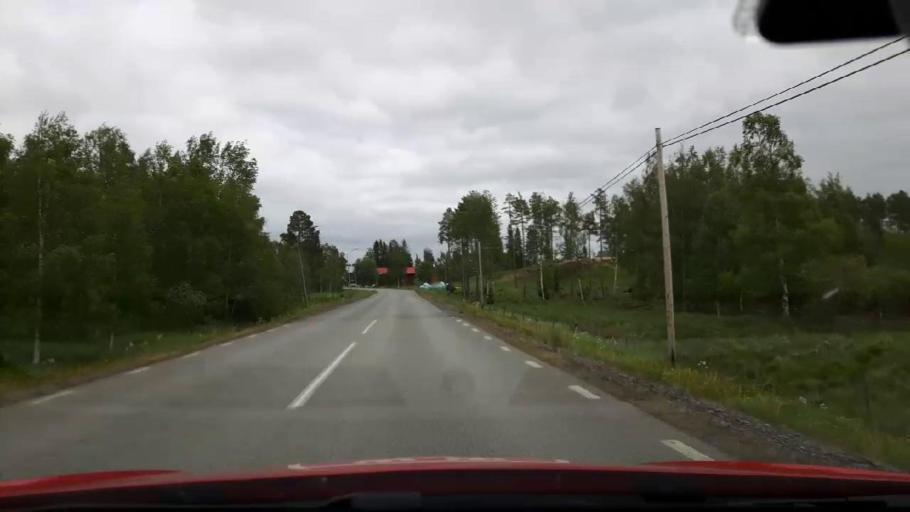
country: SE
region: Jaemtland
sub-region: OEstersunds Kommun
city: Lit
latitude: 63.6699
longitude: 15.0938
